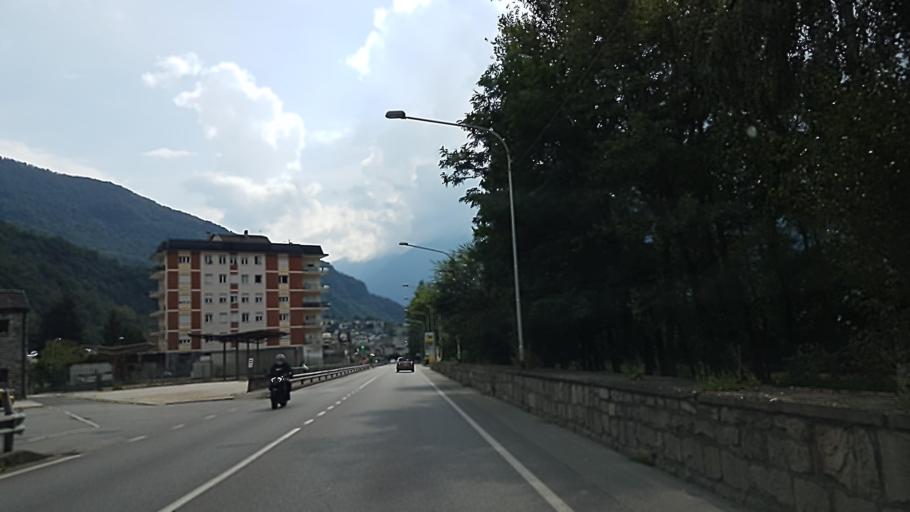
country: IT
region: Lombardy
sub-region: Provincia di Sondrio
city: Prata Centro
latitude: 46.3142
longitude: 9.3976
